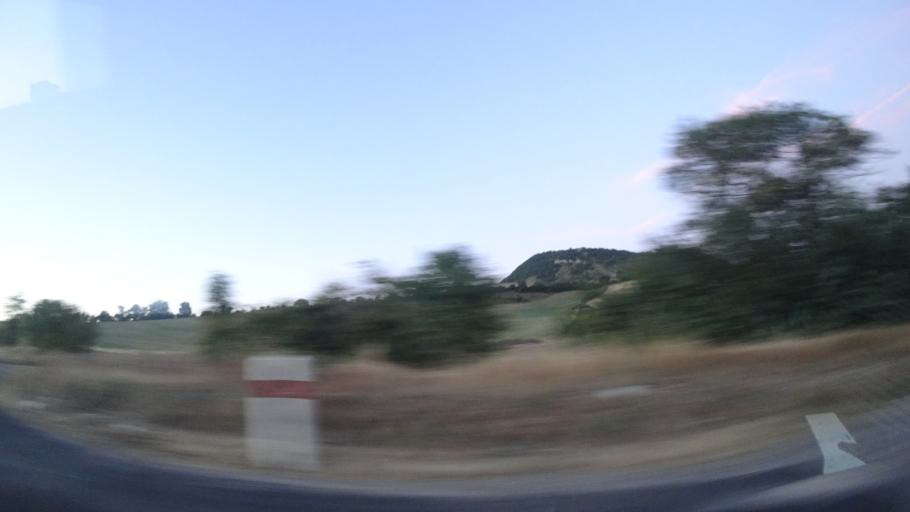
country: FR
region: Midi-Pyrenees
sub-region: Departement de l'Aveyron
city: Creissels
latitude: 44.1333
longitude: 3.0417
